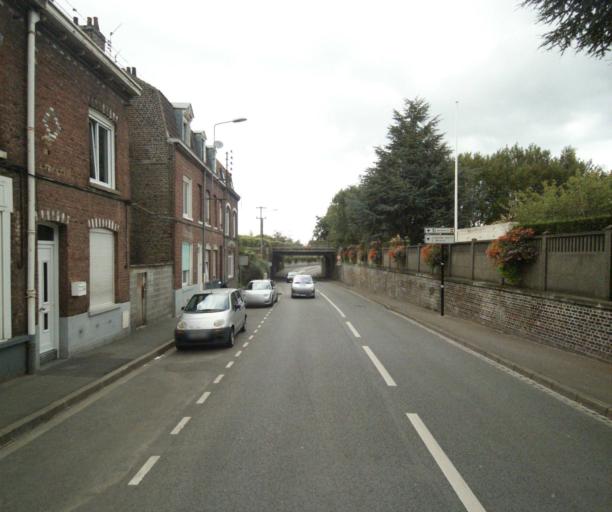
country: FR
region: Nord-Pas-de-Calais
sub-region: Departement du Nord
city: Saint-Andre-lez-Lille
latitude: 50.6601
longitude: 3.0626
